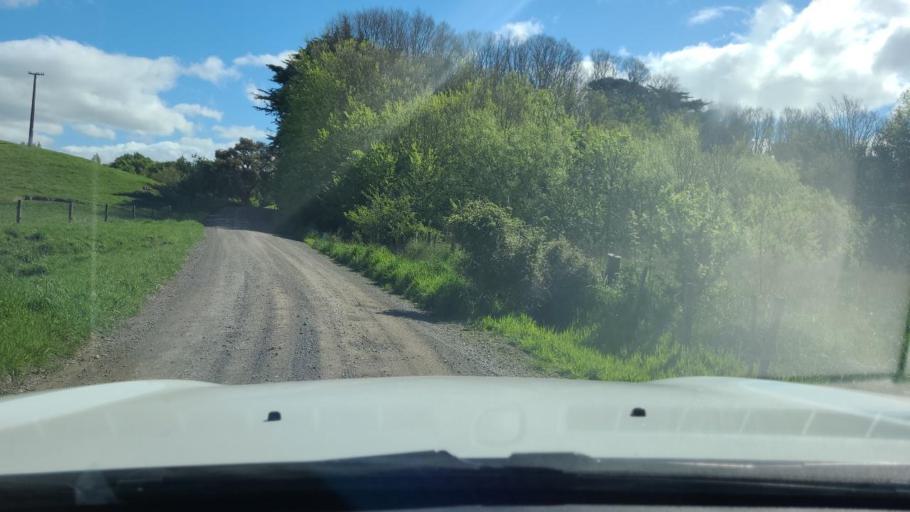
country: NZ
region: Wellington
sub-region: Upper Hutt City
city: Upper Hutt
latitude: -41.2238
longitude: 175.3111
